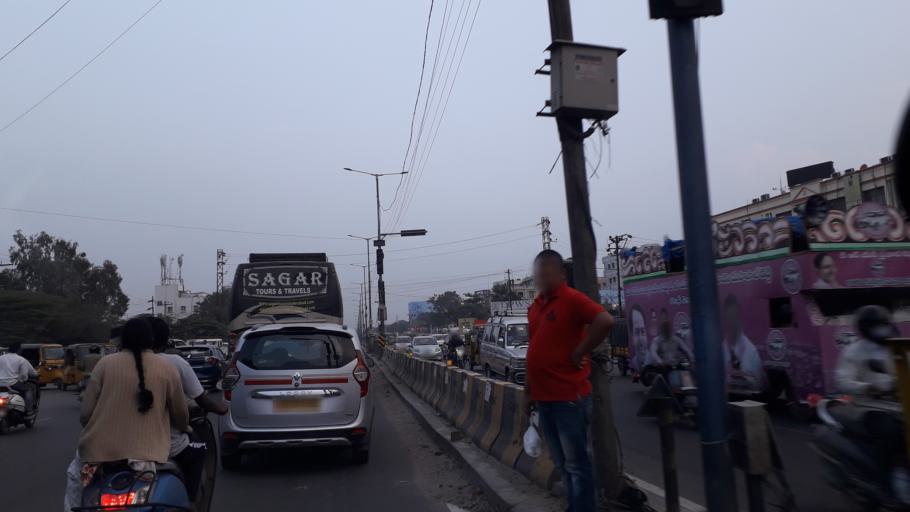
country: IN
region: Telangana
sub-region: Medak
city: Serilingampalle
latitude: 17.5092
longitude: 78.3001
